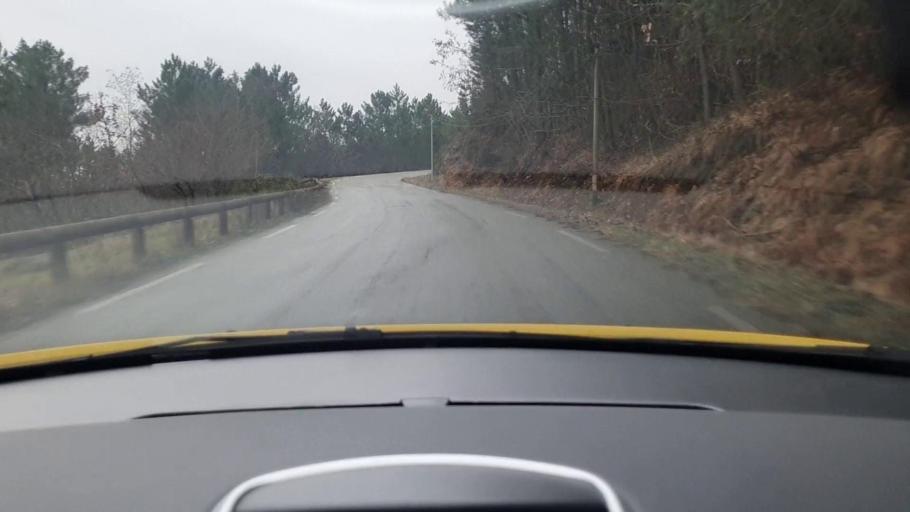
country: FR
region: Languedoc-Roussillon
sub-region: Departement du Gard
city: Besseges
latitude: 44.2755
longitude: 4.0789
